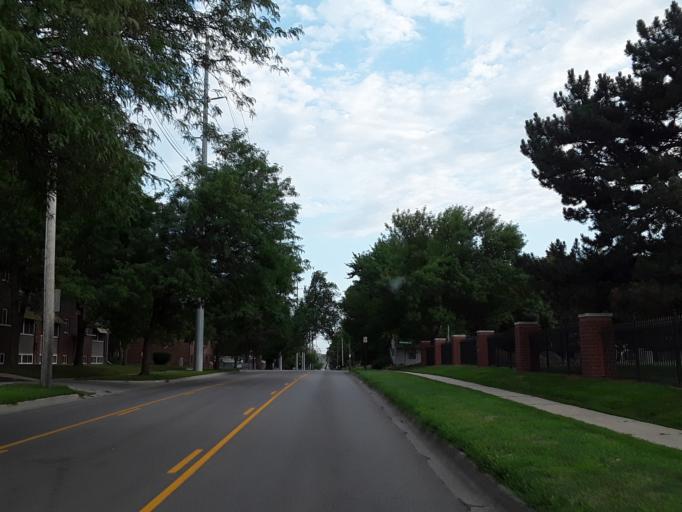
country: US
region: Nebraska
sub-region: Lancaster County
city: Lincoln
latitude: 40.8381
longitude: -96.6442
